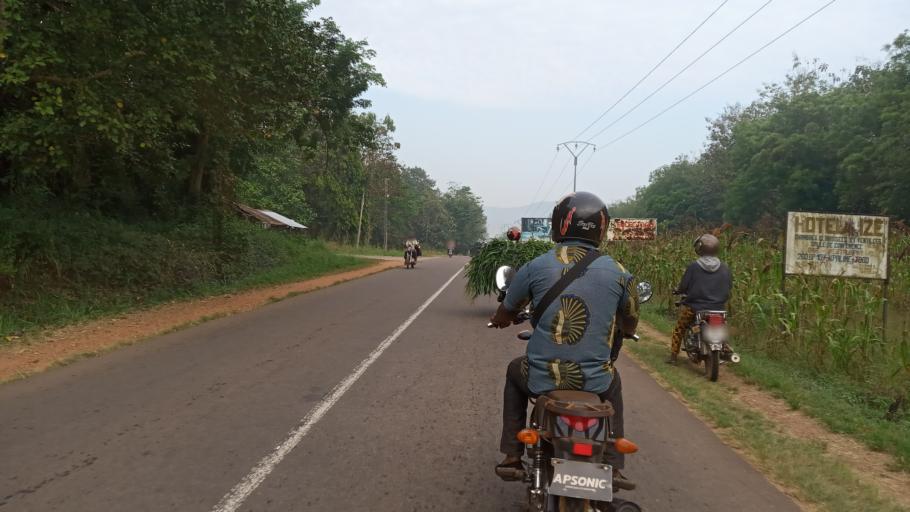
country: TG
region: Plateaux
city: Kpalime
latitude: 6.8872
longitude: 0.6439
